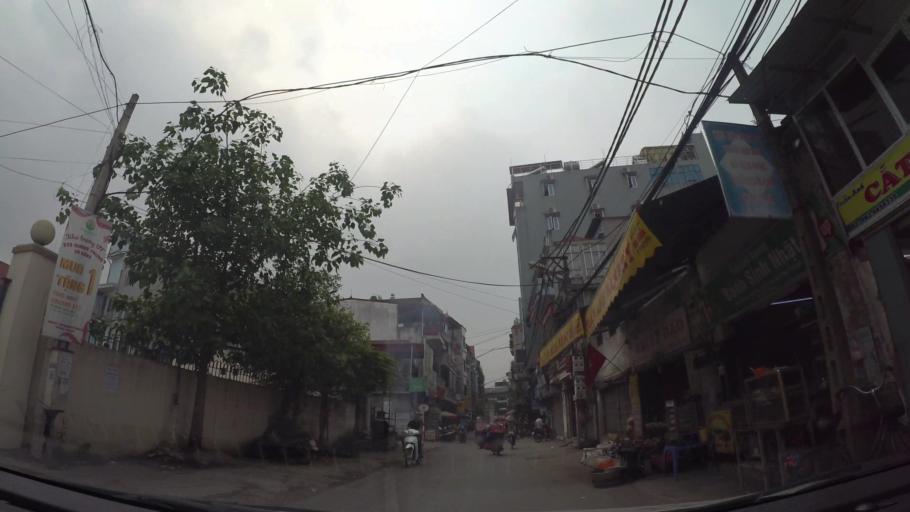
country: VN
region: Ha Noi
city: Ha Dong
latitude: 20.9655
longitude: 105.7664
